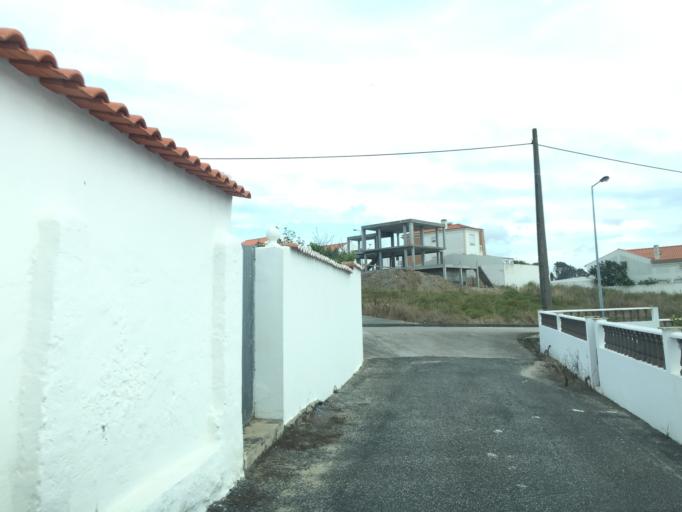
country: PT
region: Leiria
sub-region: Peniche
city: Atouguia da Baleia
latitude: 39.3501
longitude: -9.2938
